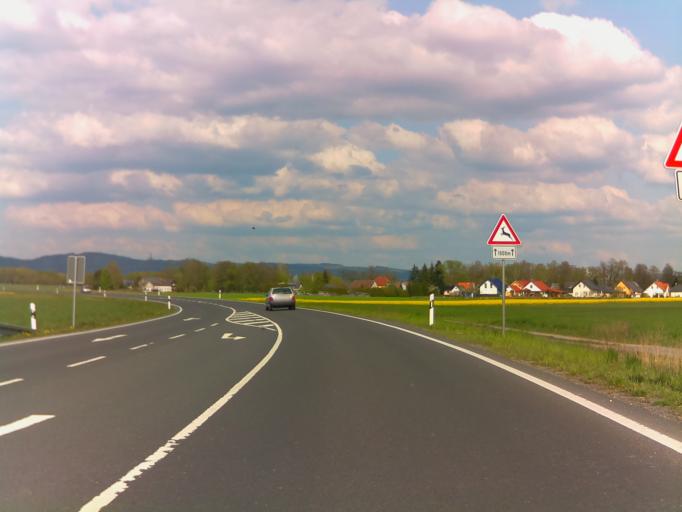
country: DE
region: Bavaria
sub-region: Upper Franconia
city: Ebersdorf
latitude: 50.3137
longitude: 11.1402
